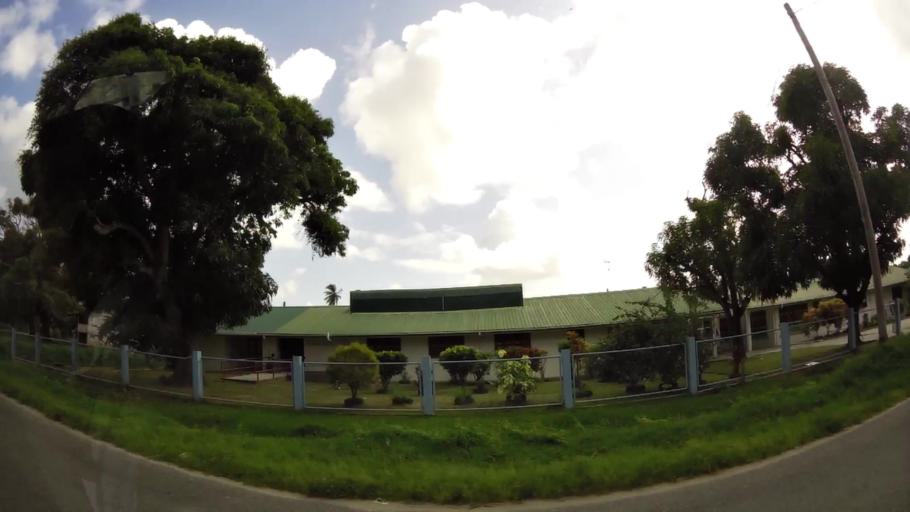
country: GY
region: Demerara-Mahaica
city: Mahaica Village
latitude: 6.7109
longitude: -57.9280
